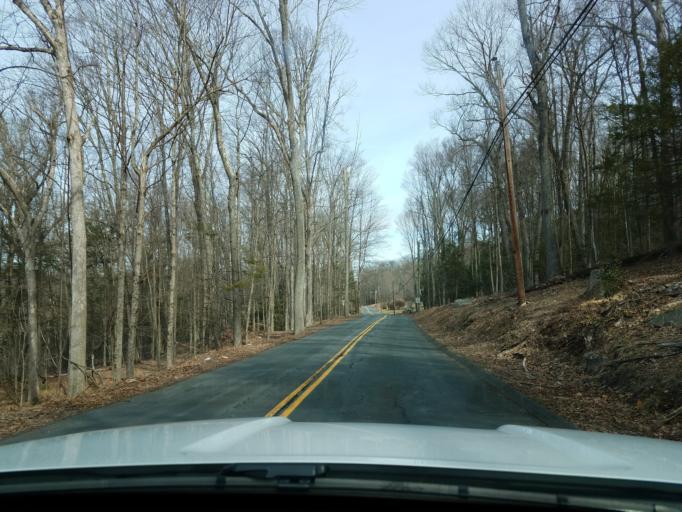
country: US
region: Connecticut
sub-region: Hartford County
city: Collinsville
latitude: 41.7885
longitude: -72.9217
